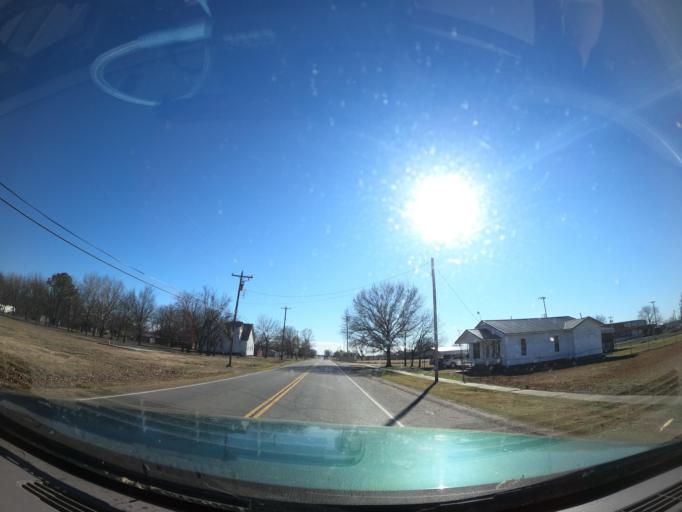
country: US
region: Oklahoma
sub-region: McIntosh County
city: Checotah
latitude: 35.5553
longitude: -95.6515
